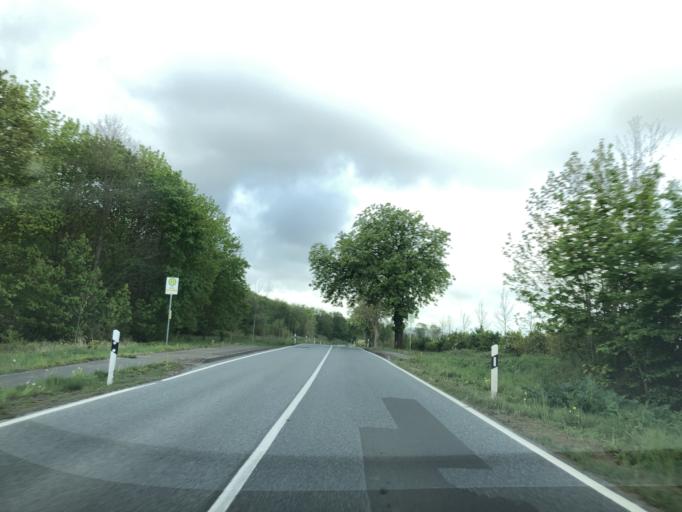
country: DE
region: Mecklenburg-Vorpommern
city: Guestrow
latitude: 53.7669
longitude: 12.1489
